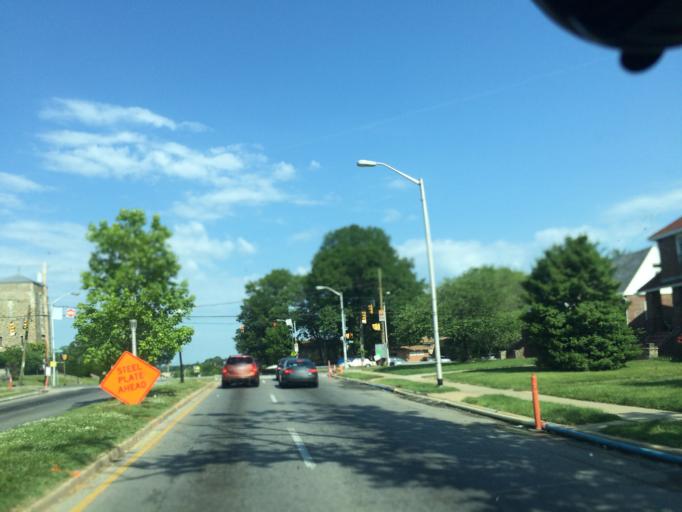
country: US
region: Maryland
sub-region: Baltimore County
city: Parkville
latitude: 39.3652
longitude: -76.5575
